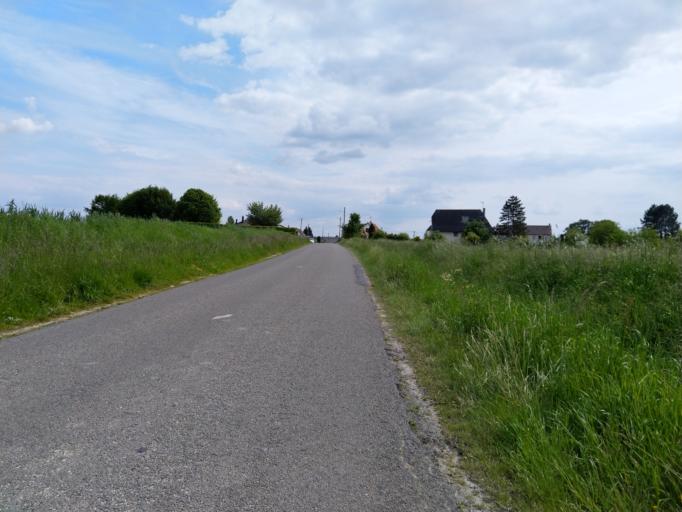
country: FR
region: Picardie
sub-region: Departement de l'Aisne
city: Boue
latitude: 50.0166
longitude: 3.6928
